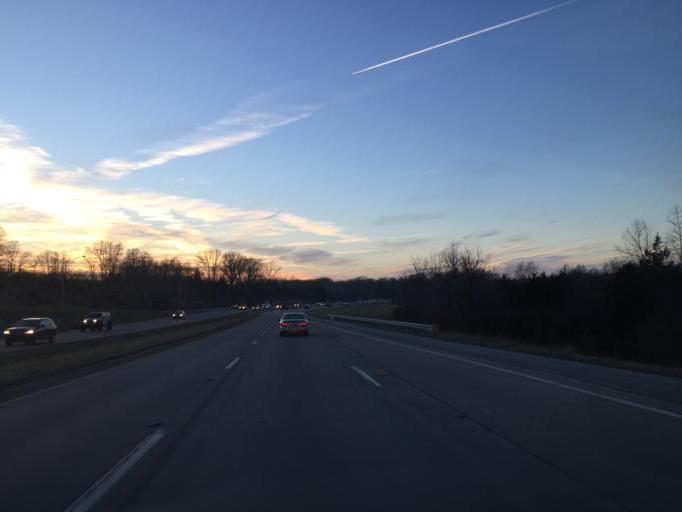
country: US
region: Indiana
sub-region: Monroe County
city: Bloomington
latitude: 39.1874
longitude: -86.5616
